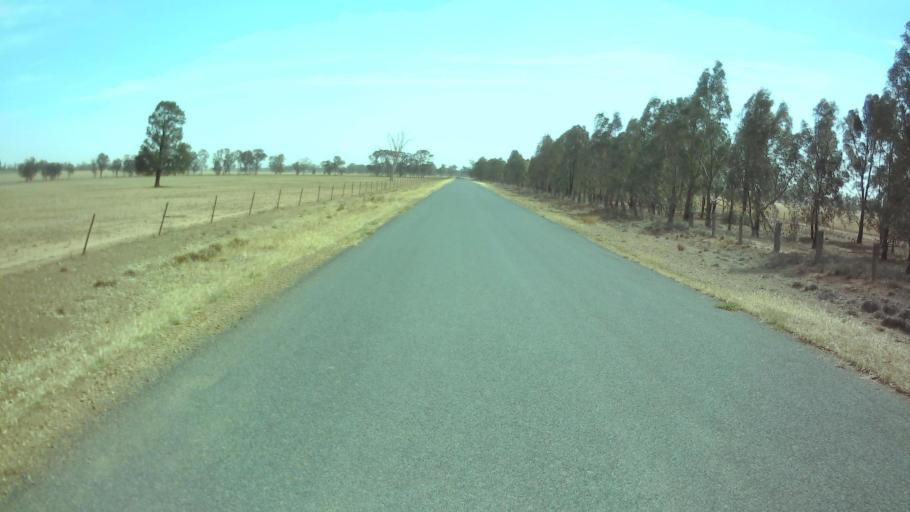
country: AU
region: New South Wales
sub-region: Weddin
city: Grenfell
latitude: -33.7144
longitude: 148.0011
